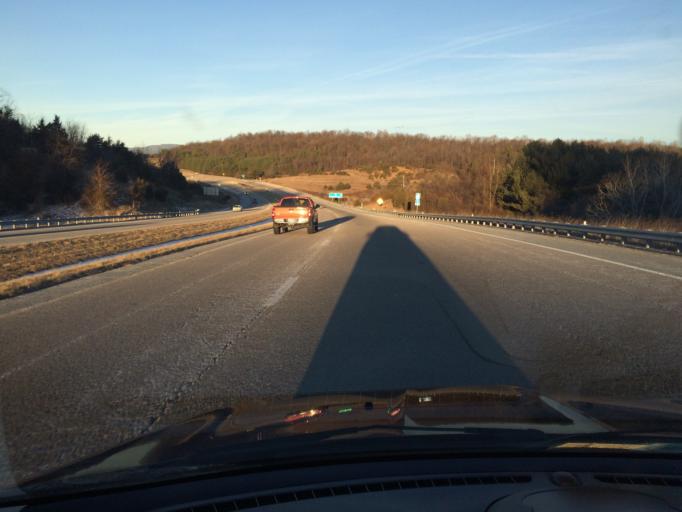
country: US
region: Virginia
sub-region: Augusta County
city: Jolivue
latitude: 38.1247
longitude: -79.0712
